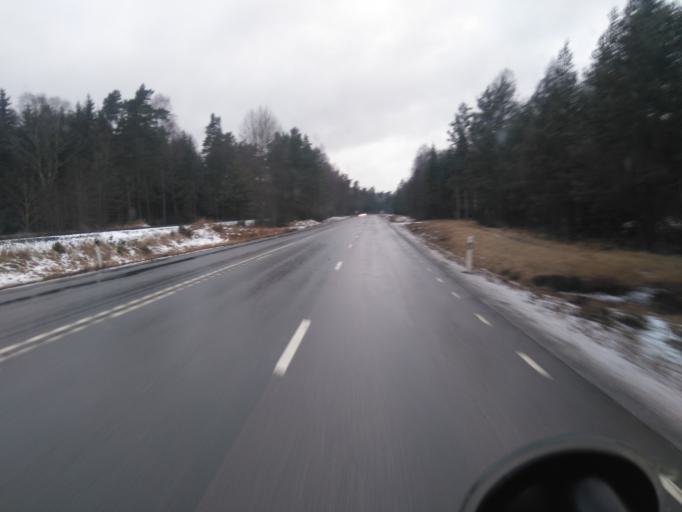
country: SE
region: Joenkoeping
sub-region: Eksjo Kommun
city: Haljarp
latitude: 57.6219
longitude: 15.4578
